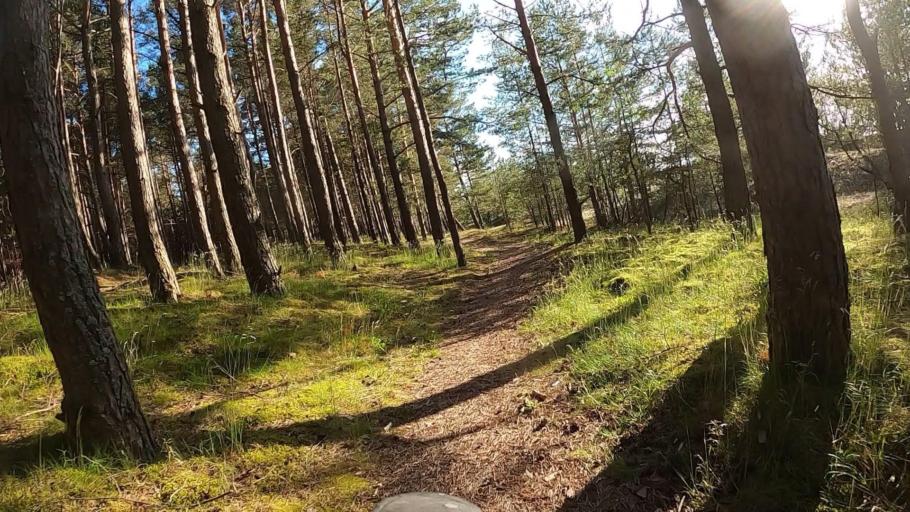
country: LV
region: Riga
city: Jaunciems
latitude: 57.1147
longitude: 24.1932
